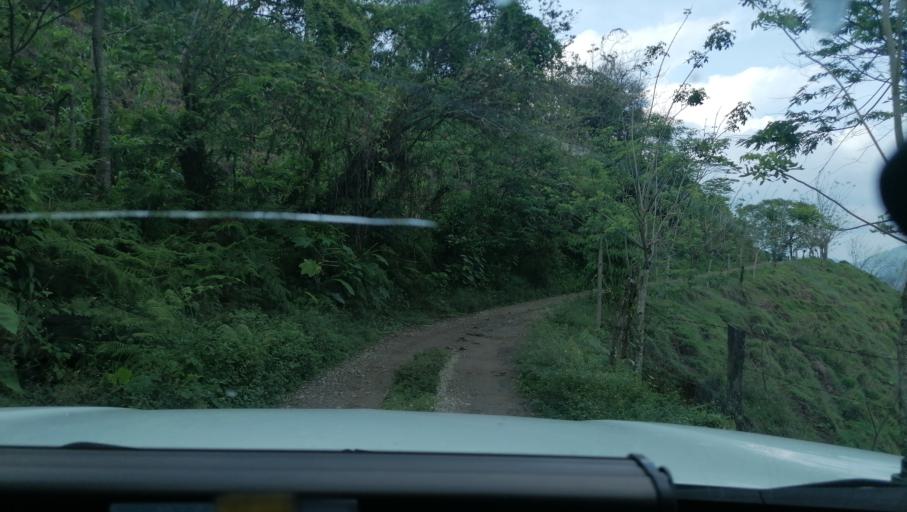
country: MX
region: Chiapas
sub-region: Tapilula
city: San Francisco Jacona
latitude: 17.3136
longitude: -93.1014
